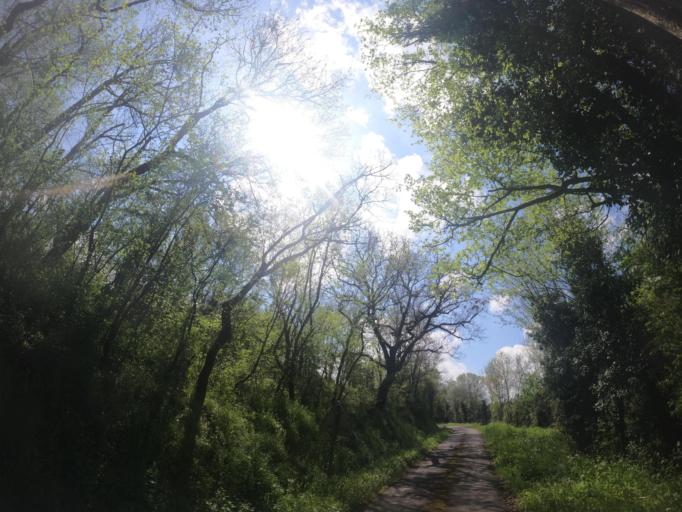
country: FR
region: Poitou-Charentes
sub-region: Departement des Deux-Sevres
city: Saint-Varent
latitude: 46.8701
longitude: -0.2451
